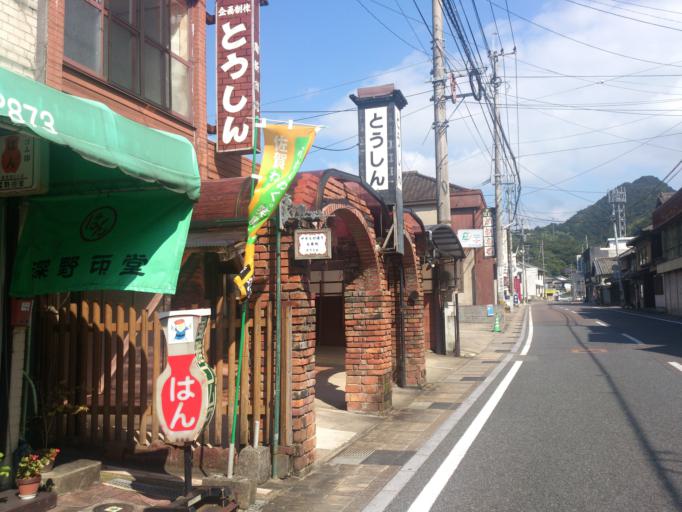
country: JP
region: Saga Prefecture
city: Imaricho-ko
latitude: 33.1819
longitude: 129.8833
